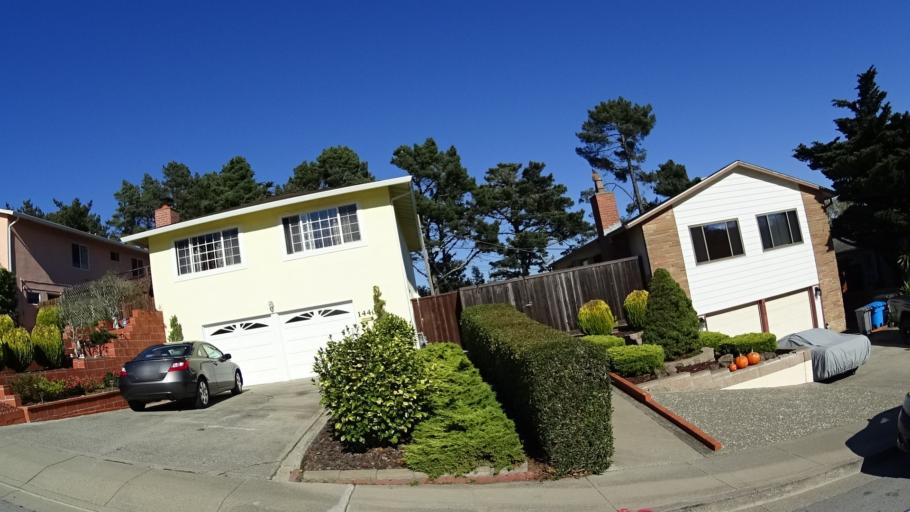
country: US
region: California
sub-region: San Mateo County
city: San Bruno
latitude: 37.6264
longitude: -122.4452
